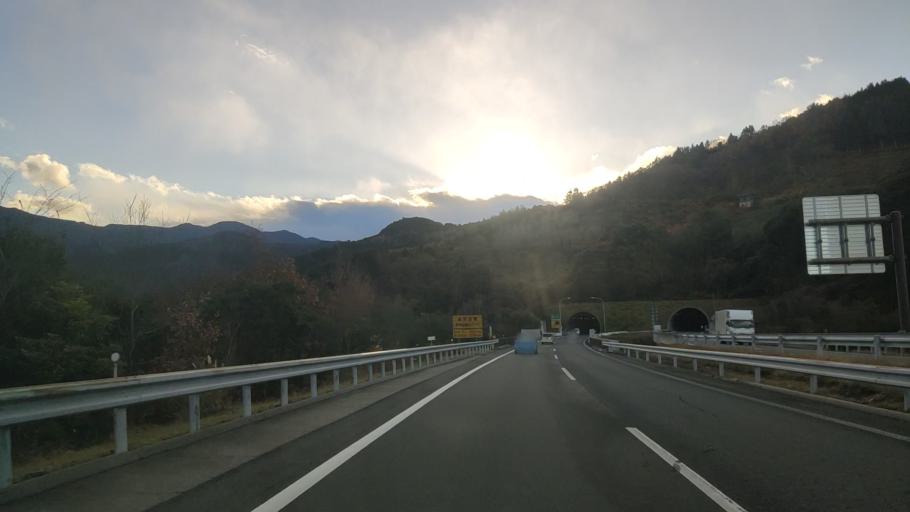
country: JP
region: Ehime
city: Saijo
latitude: 33.8767
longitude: 133.0807
